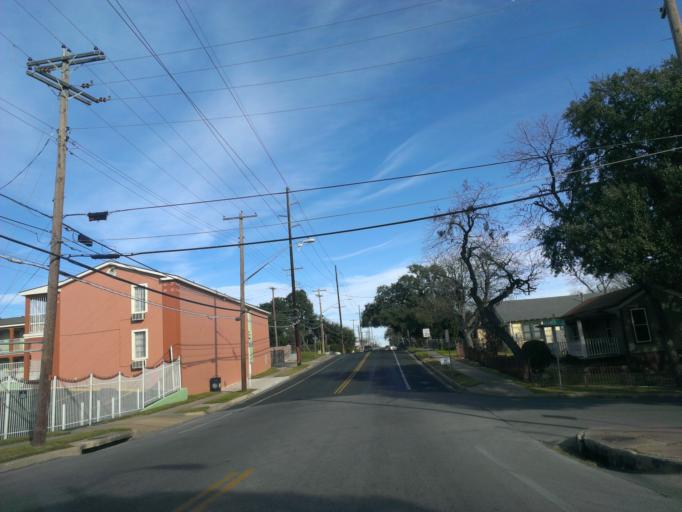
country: US
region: Texas
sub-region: Travis County
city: Austin
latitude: 30.2719
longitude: -97.7314
